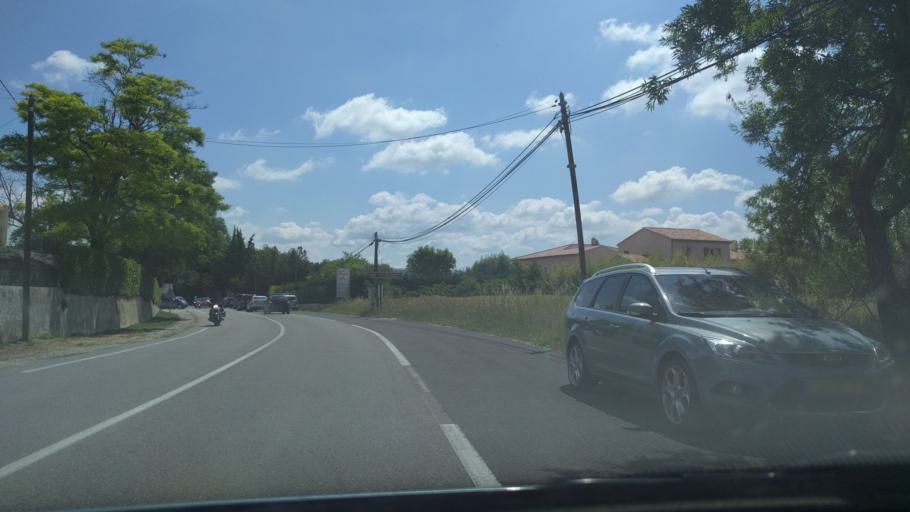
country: FR
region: Provence-Alpes-Cote d'Azur
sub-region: Departement du Vaucluse
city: Ansouis
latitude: 43.7577
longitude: 5.5034
